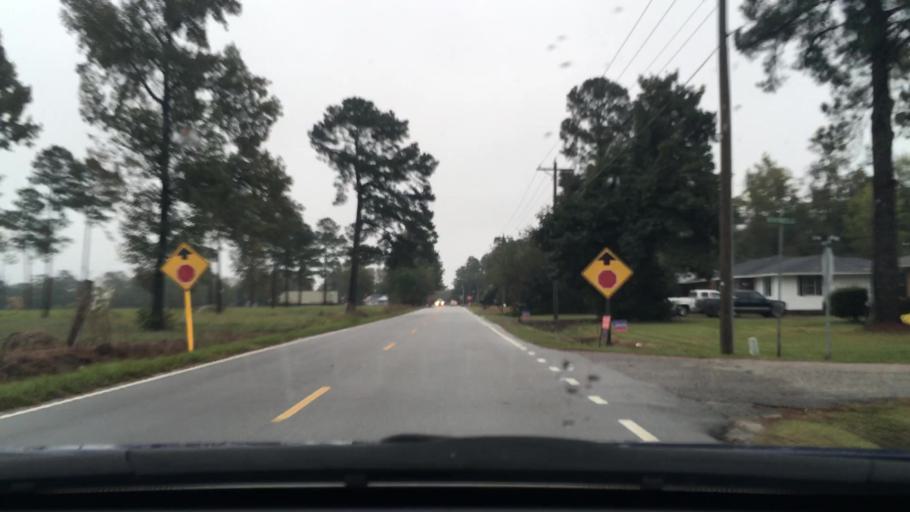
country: US
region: South Carolina
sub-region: Darlington County
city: Darlington
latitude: 34.2868
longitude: -79.9134
